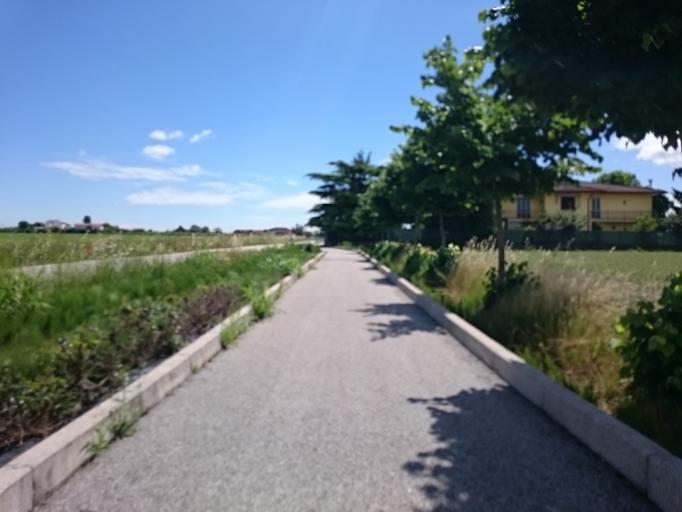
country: IT
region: Veneto
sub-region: Provincia di Padova
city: Polverara
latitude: 45.3201
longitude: 11.9478
